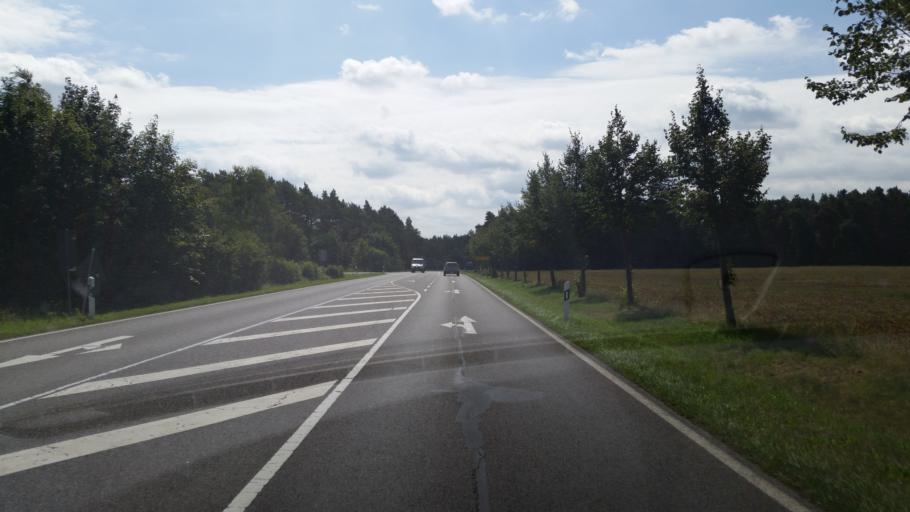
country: DE
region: Saxony
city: Kamenz
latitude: 51.3139
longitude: 14.0917
